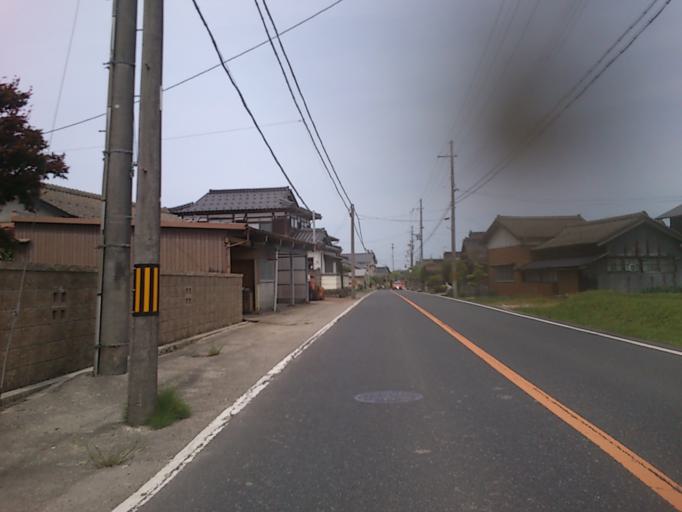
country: JP
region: Kyoto
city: Miyazu
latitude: 35.5976
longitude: 135.0948
